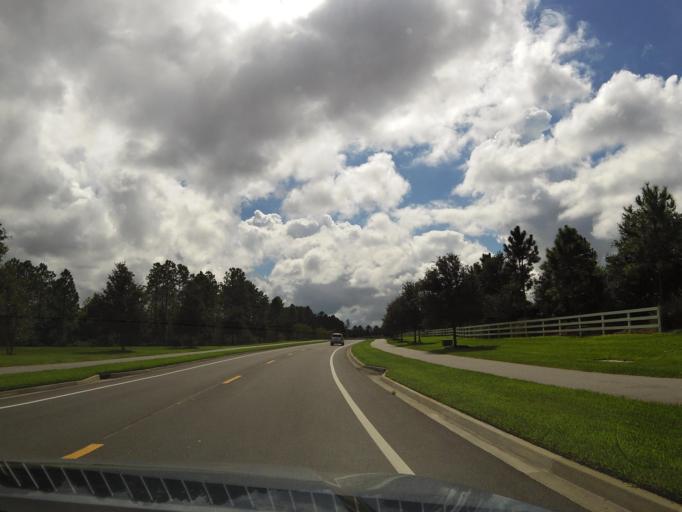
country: US
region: Florida
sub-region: Saint Johns County
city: Palm Valley
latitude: 30.0697
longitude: -81.3996
